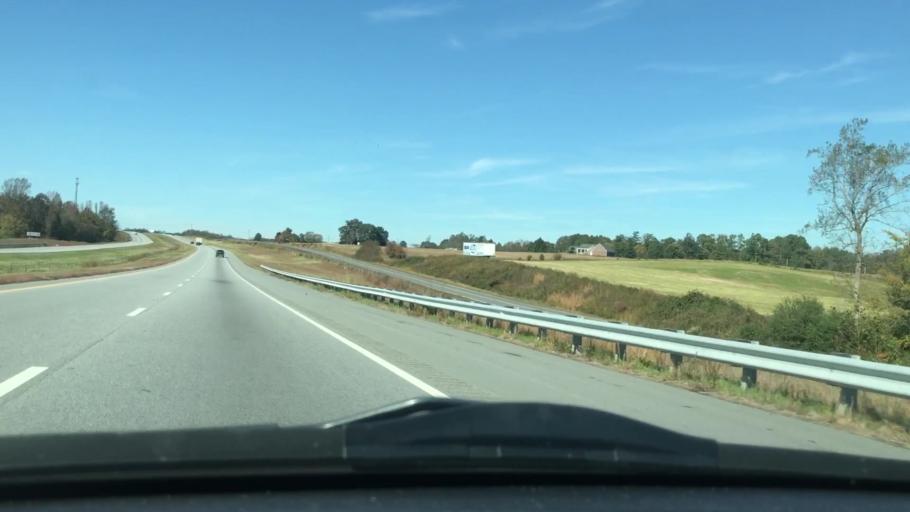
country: US
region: North Carolina
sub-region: Randolph County
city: Randleman
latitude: 35.8631
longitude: -79.8892
